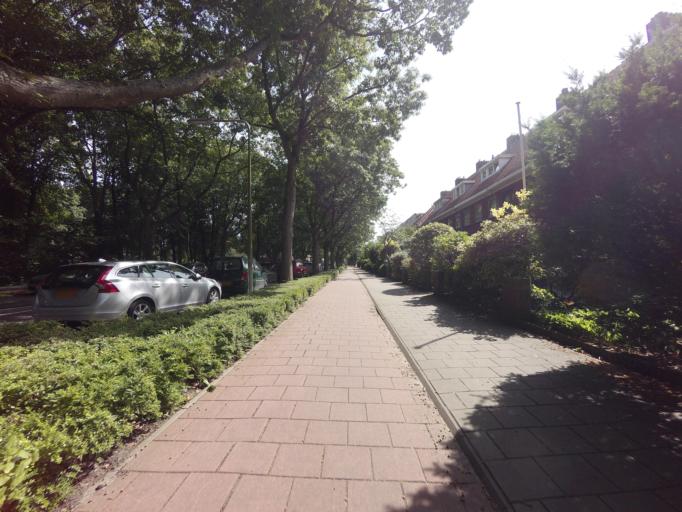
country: NL
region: South Holland
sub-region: Gemeente Wassenaar
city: Wassenaar
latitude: 52.1451
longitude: 4.3887
